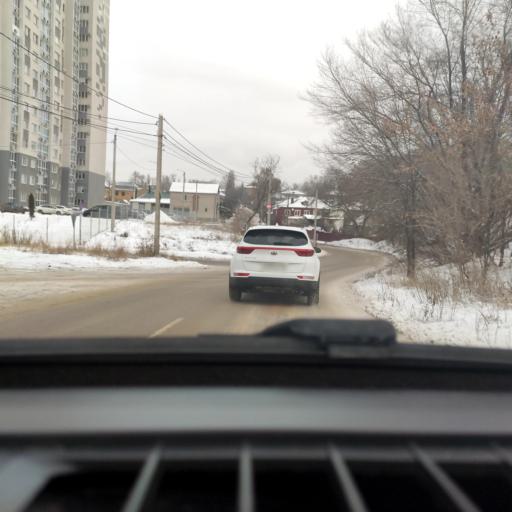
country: RU
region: Voronezj
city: Voronezh
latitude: 51.6716
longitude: 39.1360
